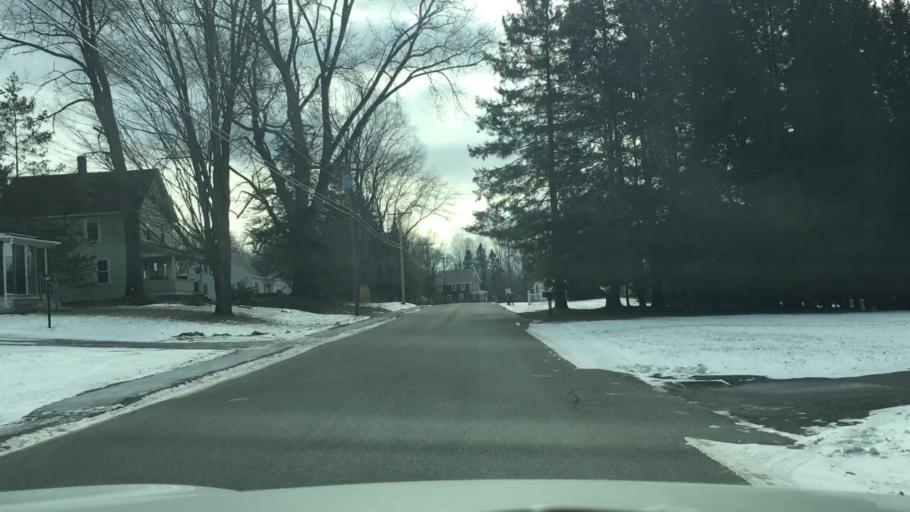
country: US
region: Massachusetts
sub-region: Berkshire County
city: Lee
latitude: 42.3297
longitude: -73.2378
